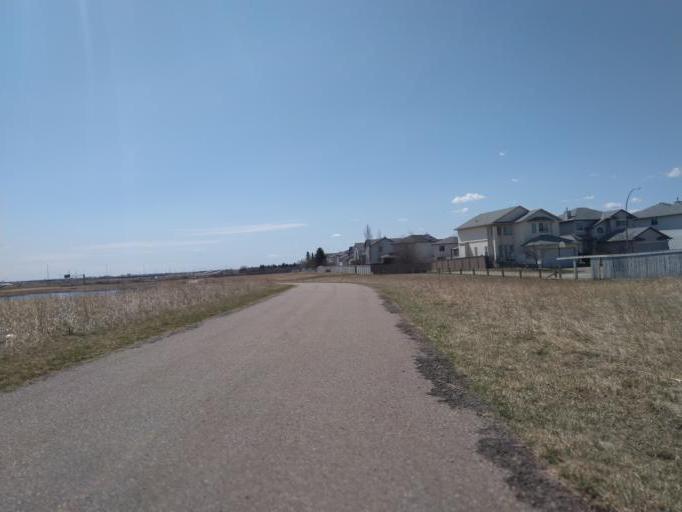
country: CA
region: Alberta
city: Chestermere
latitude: 51.0895
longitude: -113.9240
